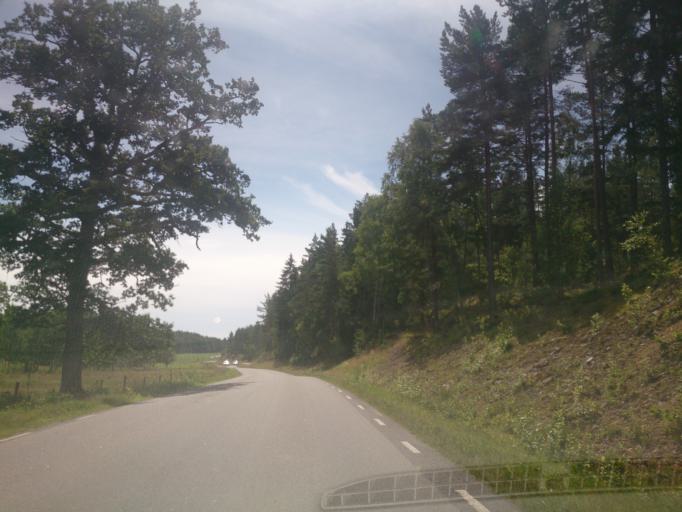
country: SE
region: OEstergoetland
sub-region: Valdemarsviks Kommun
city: Valdemarsvik
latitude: 58.3091
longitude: 16.6518
